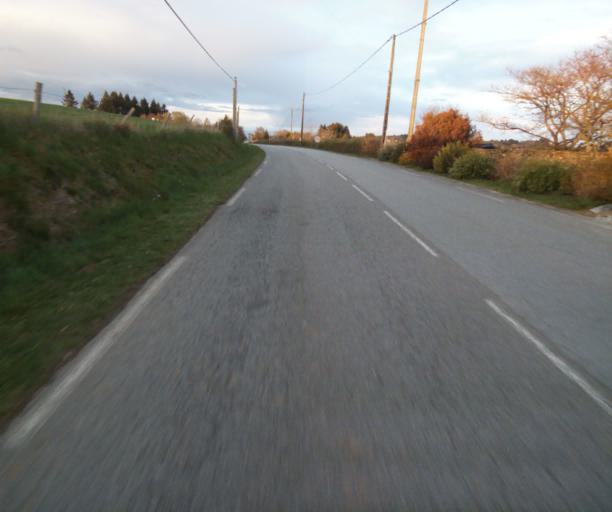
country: FR
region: Limousin
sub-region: Departement de la Correze
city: Laguenne
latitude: 45.2768
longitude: 1.8256
